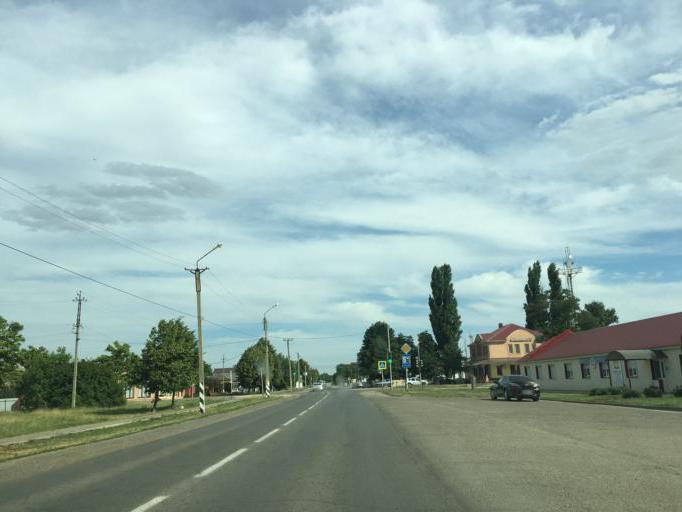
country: RU
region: Krasnodarskiy
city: Kushchevskaya
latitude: 46.5480
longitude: 39.6180
